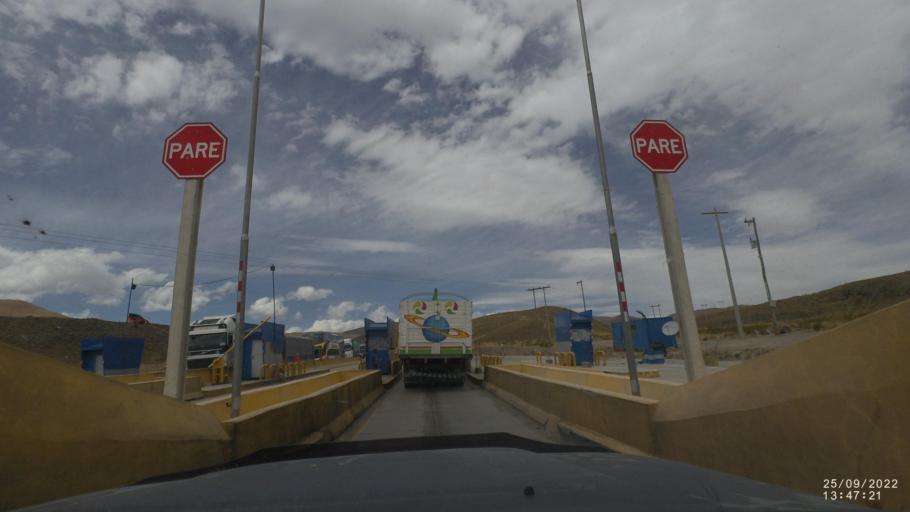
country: BO
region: La Paz
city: Colquiri
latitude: -17.6663
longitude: -67.0217
